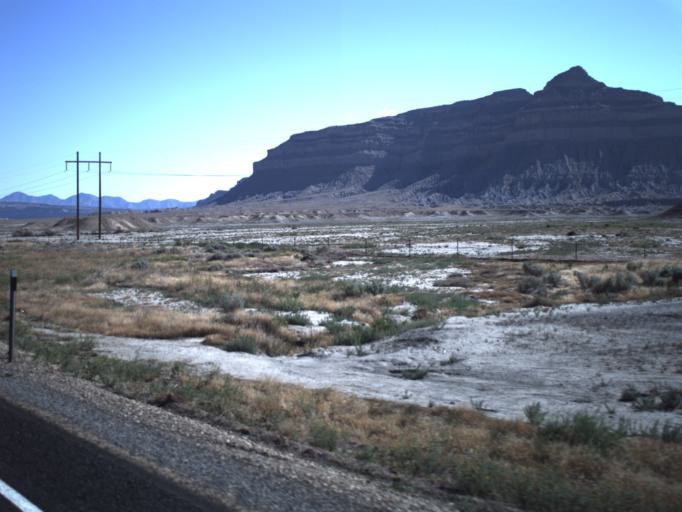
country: US
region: Utah
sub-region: Carbon County
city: East Carbon City
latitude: 39.1591
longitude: -110.3381
